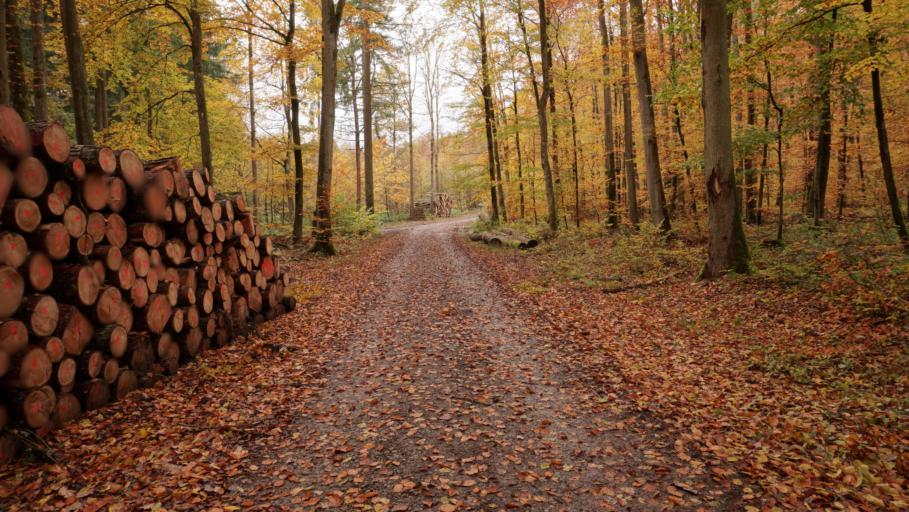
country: DE
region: Baden-Wuerttemberg
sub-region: Karlsruhe Region
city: Mosbach
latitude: 49.3370
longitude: 9.1944
